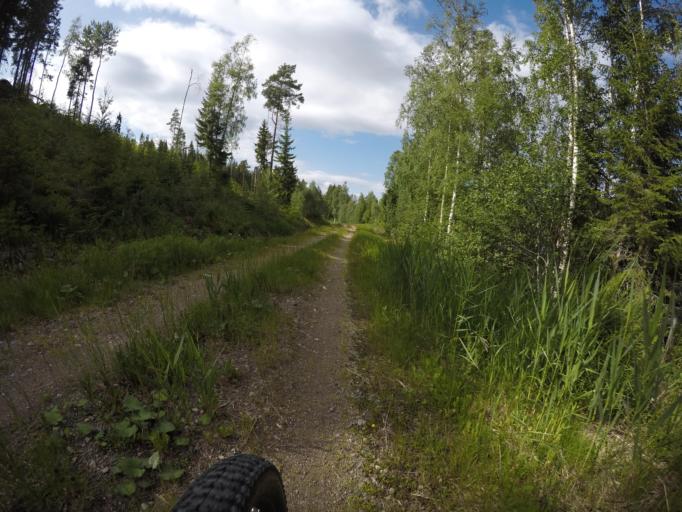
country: SE
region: Dalarna
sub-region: Ludvika Kommun
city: Abborrberget
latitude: 60.0486
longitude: 14.5901
